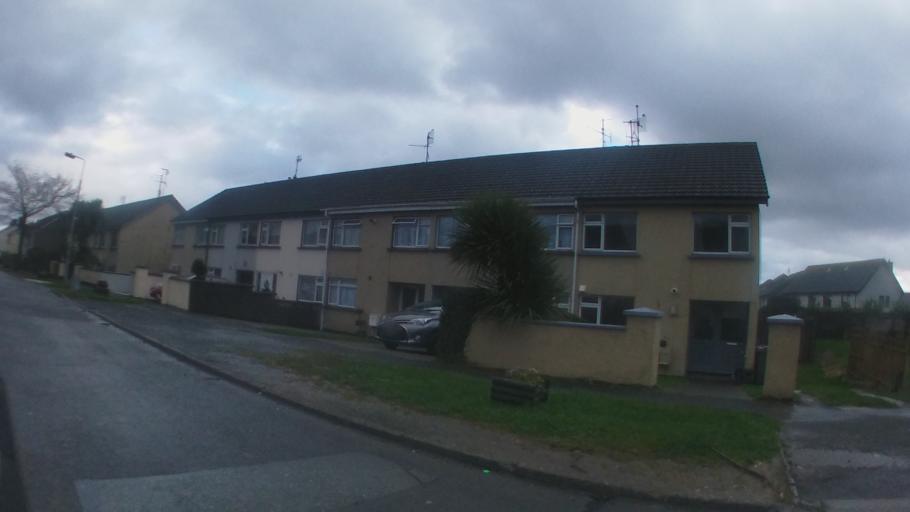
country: IE
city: Newtownmountkennedy
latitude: 53.0859
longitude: -6.1122
